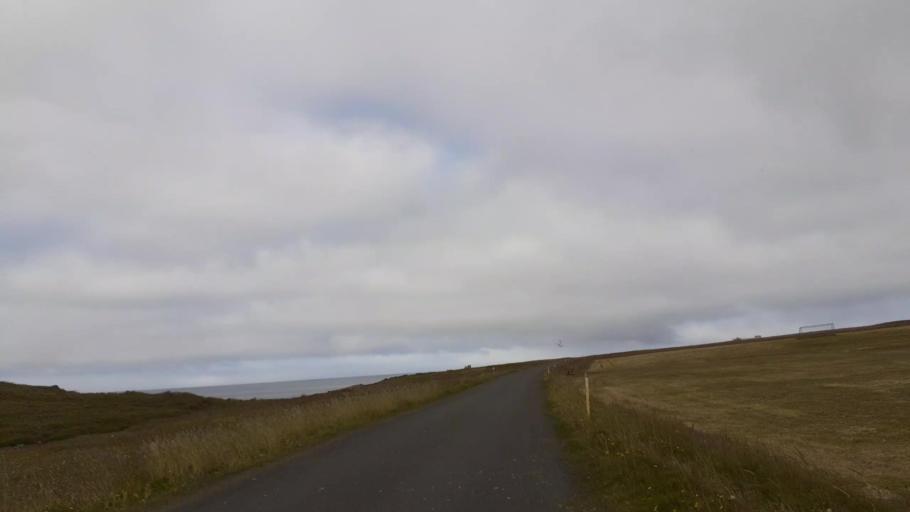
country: IS
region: Northeast
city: Dalvik
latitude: 66.5428
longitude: -18.0176
